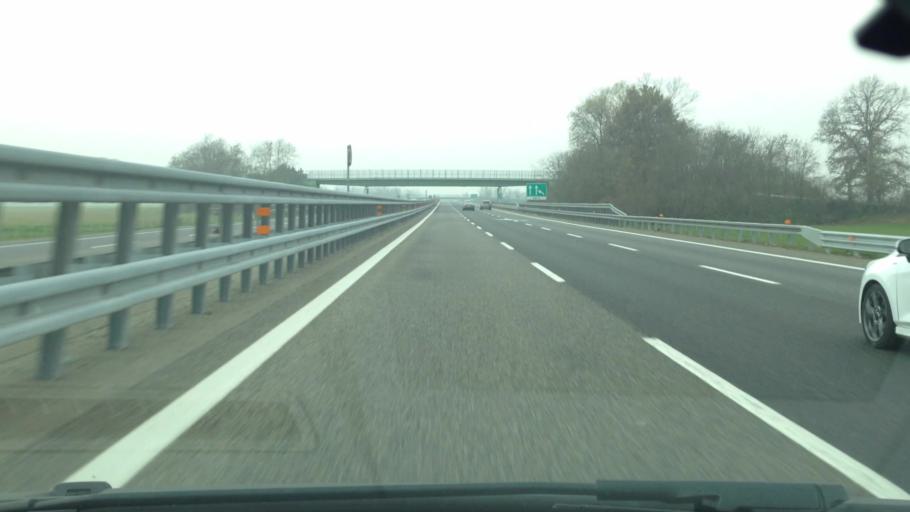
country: IT
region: Piedmont
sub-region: Provincia di Torino
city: Pessione
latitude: 44.9577
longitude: 7.8301
